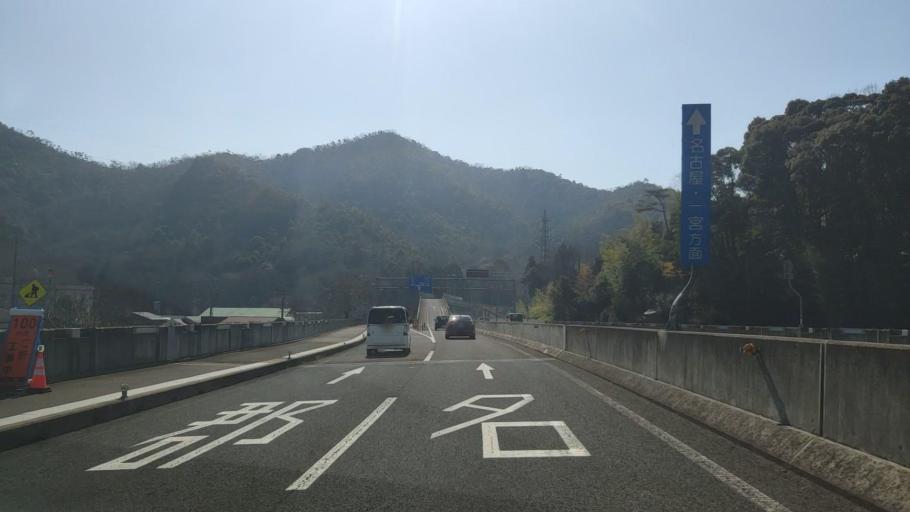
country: JP
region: Gifu
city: Gifu-shi
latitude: 35.4299
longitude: 136.7958
